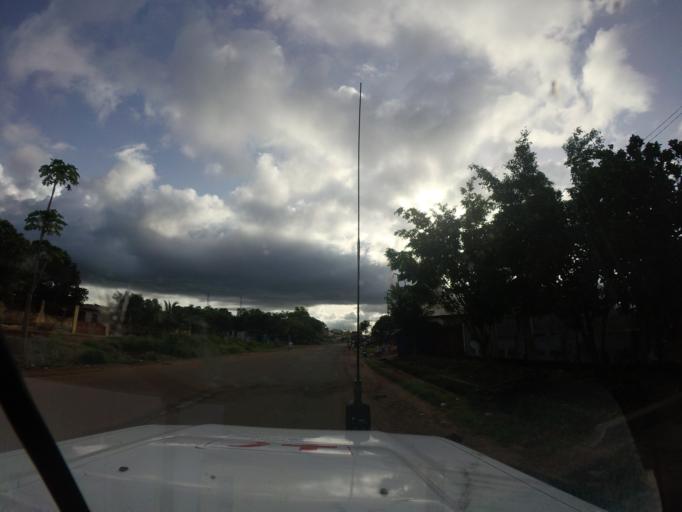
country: GN
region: Kindia
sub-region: Kindia
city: Kindia
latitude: 10.0171
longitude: -12.8865
